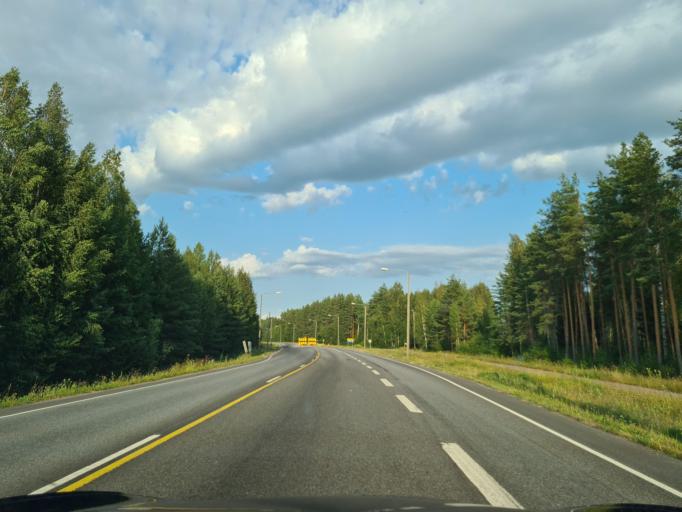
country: FI
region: Southern Ostrobothnia
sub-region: Seinaejoki
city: Lapua
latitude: 62.9866
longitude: 22.9366
